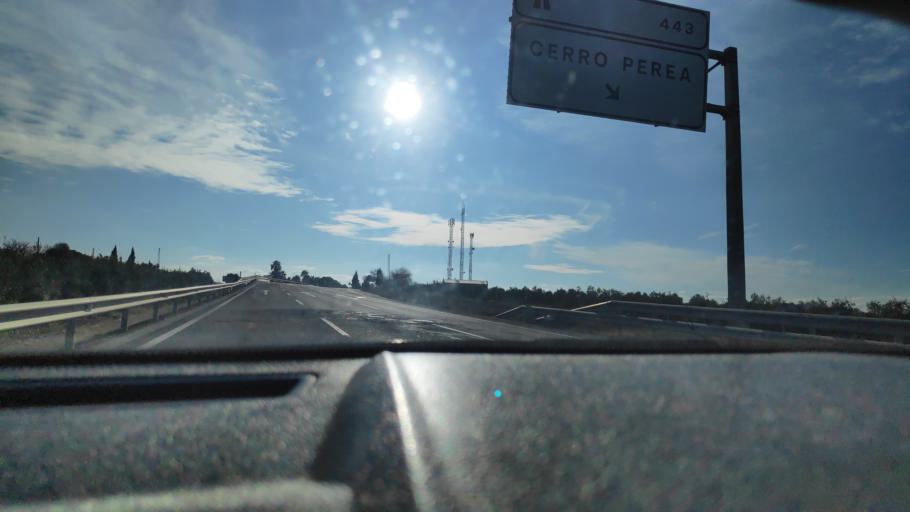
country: ES
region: Andalusia
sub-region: Province of Cordoba
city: La Carlota
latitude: 37.5931
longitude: -4.9788
